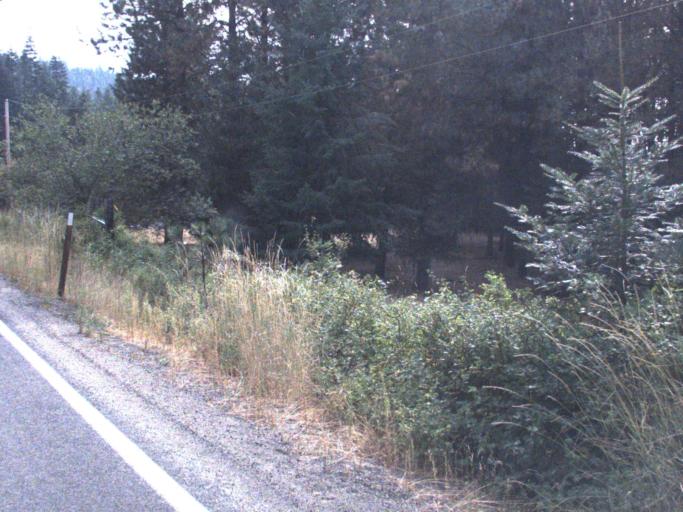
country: US
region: Washington
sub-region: Spokane County
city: Trentwood
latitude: 47.8328
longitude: -117.1997
